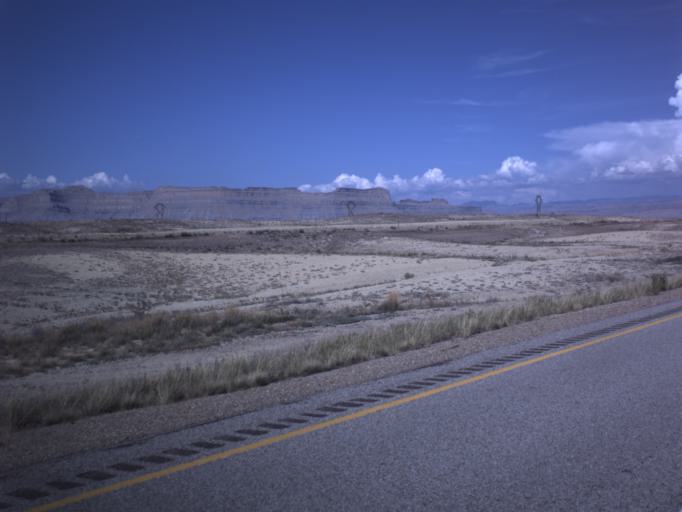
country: US
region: Utah
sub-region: Carbon County
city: East Carbon City
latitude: 38.9636
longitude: -110.2809
